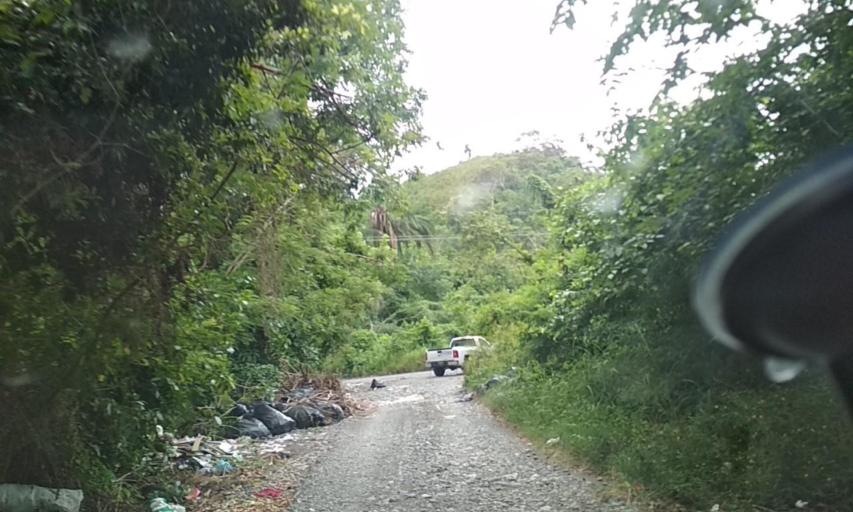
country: MX
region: Veracruz
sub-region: Papantla
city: Residencial Tajin
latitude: 20.6333
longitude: -97.3805
